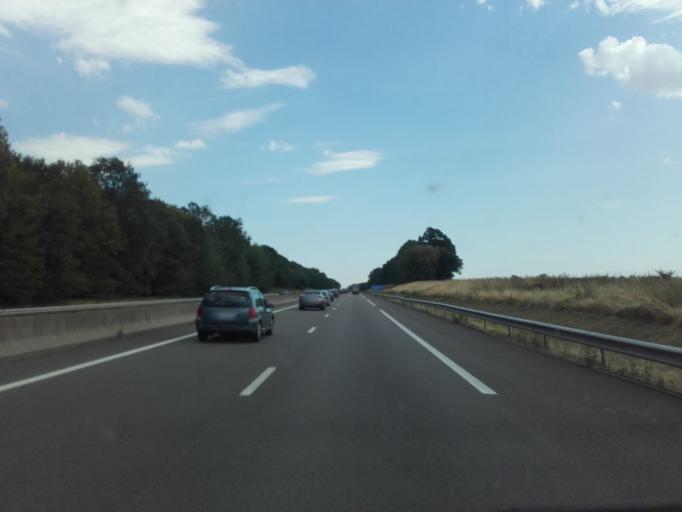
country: FR
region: Bourgogne
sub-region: Departement de la Cote-d'Or
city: Semur-en-Auxois
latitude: 47.4618
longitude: 4.2519
